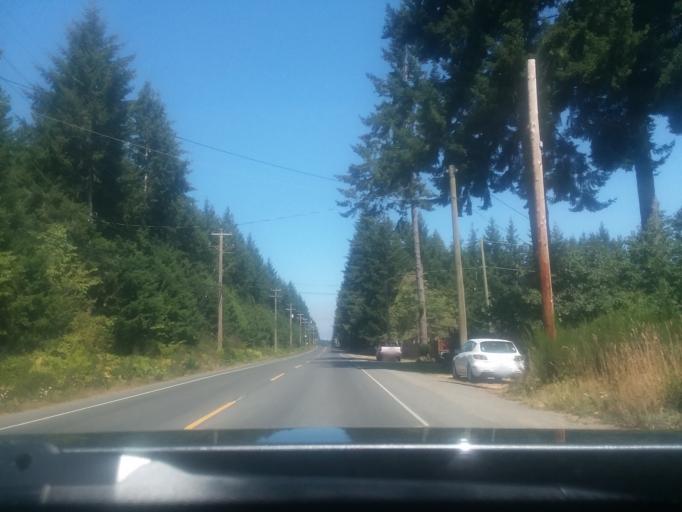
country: CA
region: British Columbia
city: Courtenay
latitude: 49.7109
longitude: -124.9338
